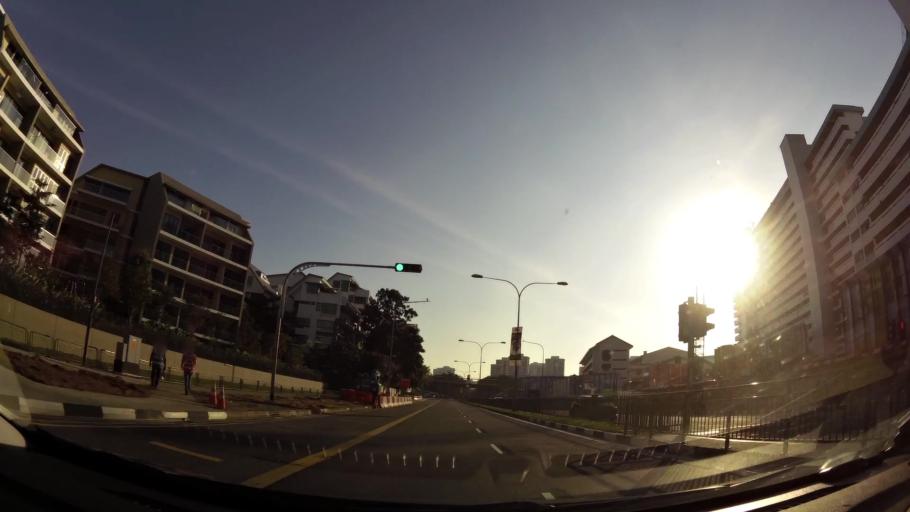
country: SG
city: Singapore
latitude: 1.3069
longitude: 103.9155
